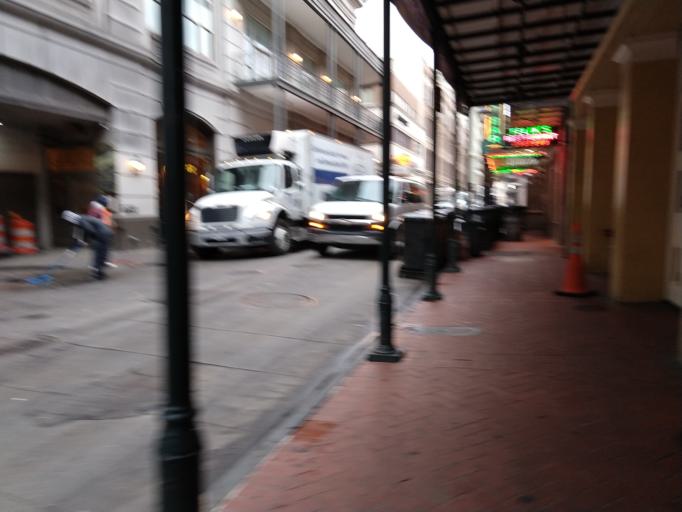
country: US
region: Louisiana
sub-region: Orleans Parish
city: New Orleans
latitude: 29.9542
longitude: -90.0687
